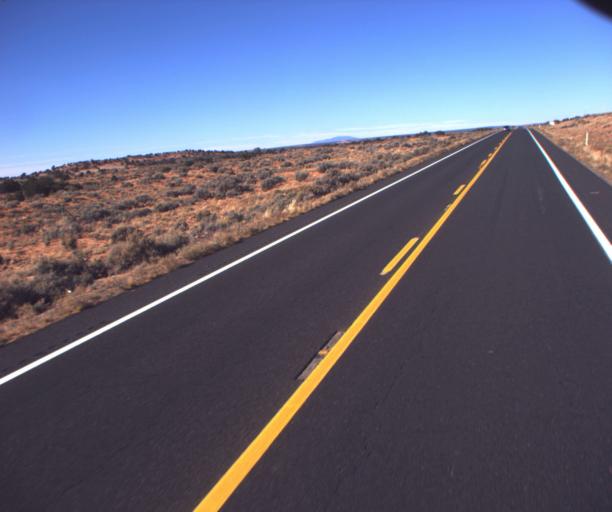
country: US
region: Arizona
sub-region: Coconino County
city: Kaibito
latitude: 36.5312
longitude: -110.7013
